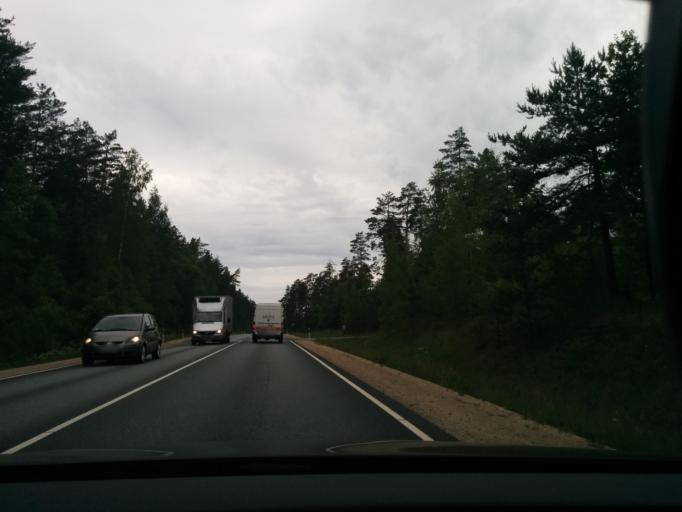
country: LV
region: Ikskile
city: Ikskile
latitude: 56.8931
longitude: 24.4486
